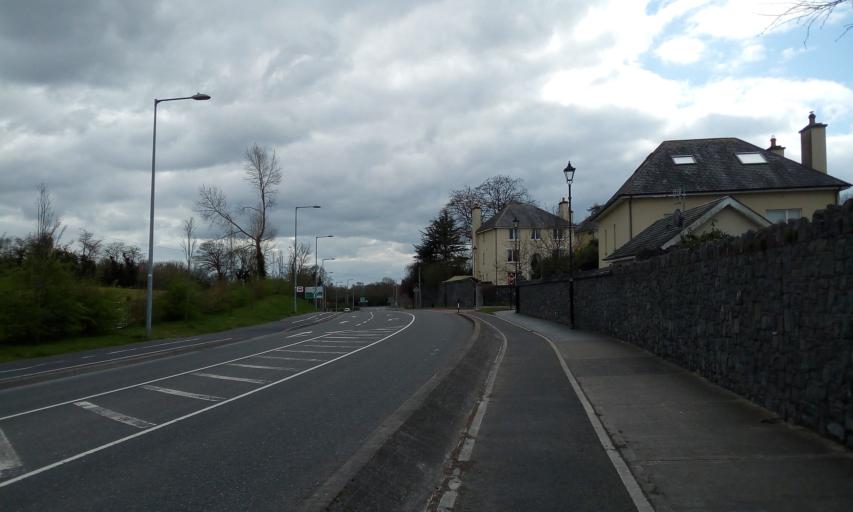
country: IE
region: Leinster
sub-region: Kilkenny
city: Kilkenny
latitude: 52.6405
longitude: -7.2566
